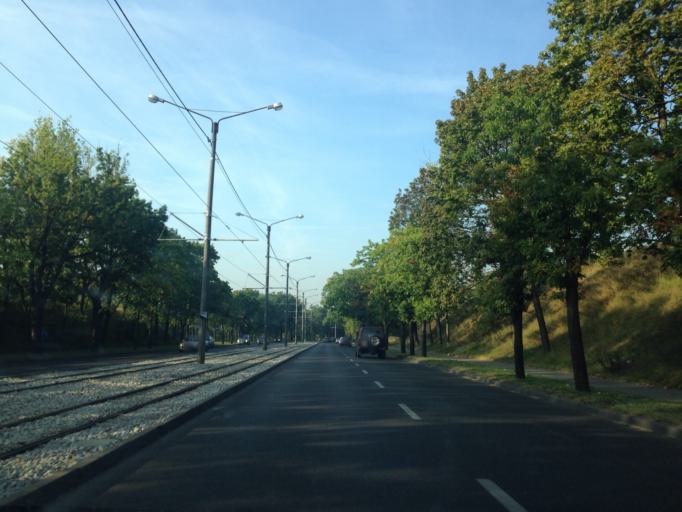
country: PL
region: Kujawsko-Pomorskie
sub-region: Torun
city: Torun
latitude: 53.0136
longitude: 18.6272
